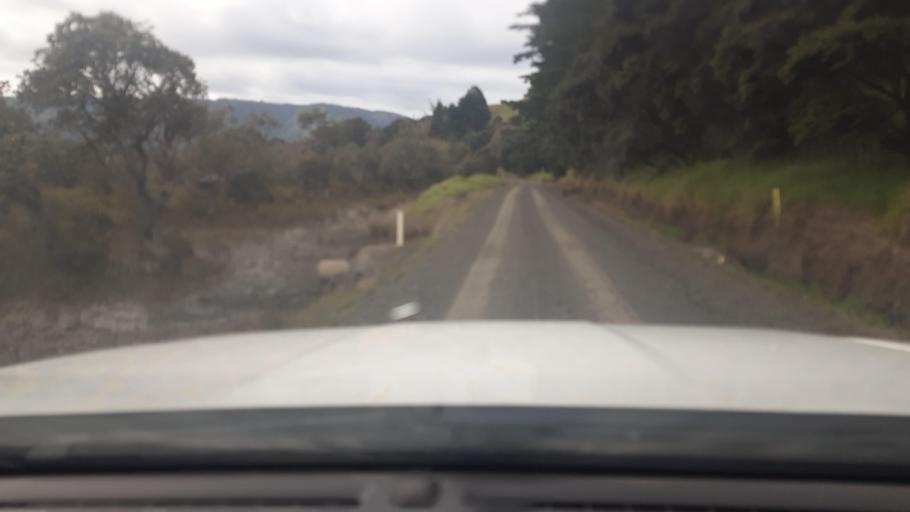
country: NZ
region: Northland
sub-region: Far North District
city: Ahipara
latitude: -35.3374
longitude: 173.2242
